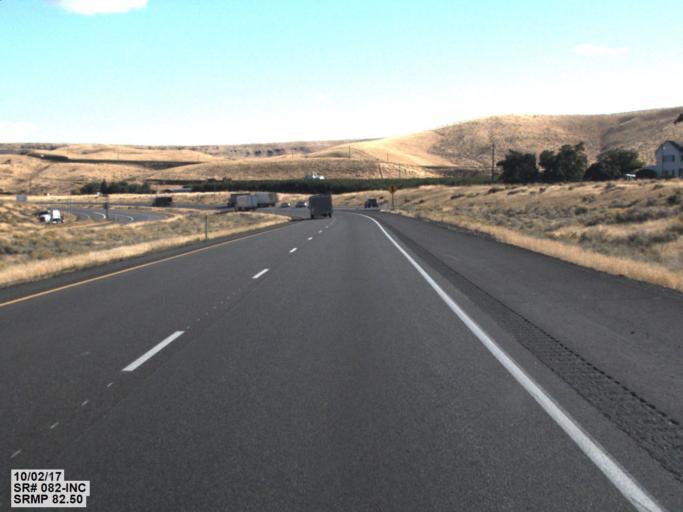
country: US
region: Washington
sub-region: Benton County
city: Prosser
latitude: 46.2132
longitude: -119.7417
